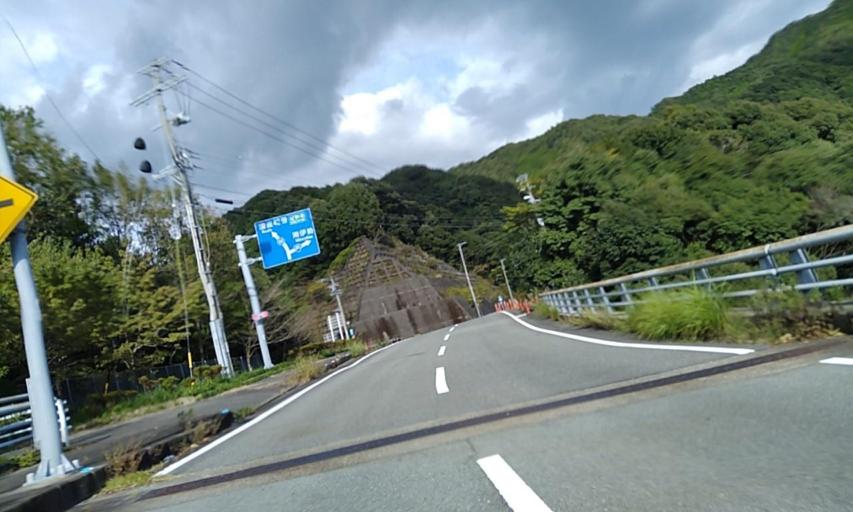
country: JP
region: Mie
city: Owase
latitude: 34.2495
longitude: 136.4036
